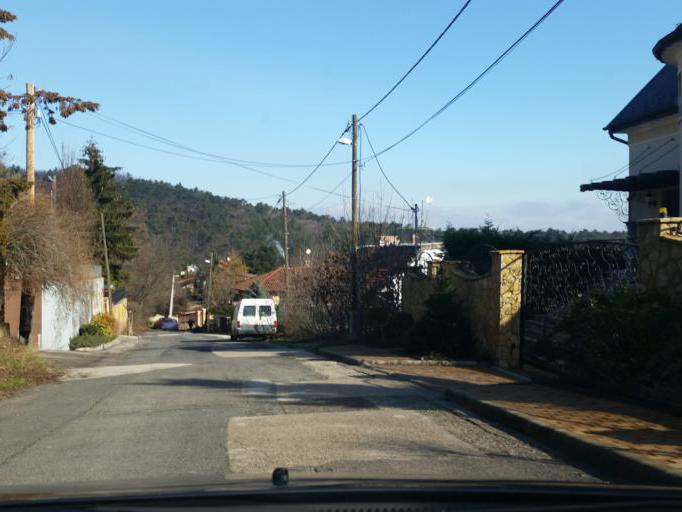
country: HU
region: Budapest
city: Budapest II. keruelet
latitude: 47.5370
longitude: 19.0094
